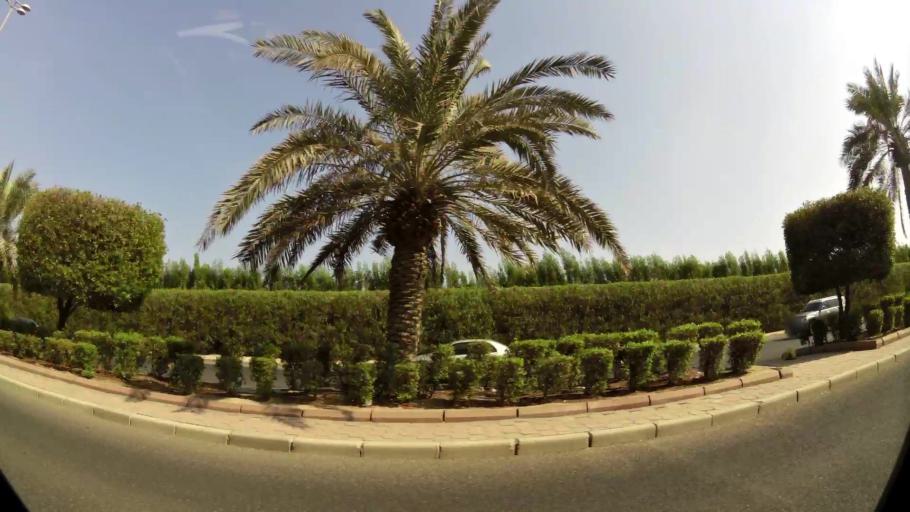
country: KW
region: Al Ahmadi
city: Al Manqaf
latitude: 29.1097
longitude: 48.1366
